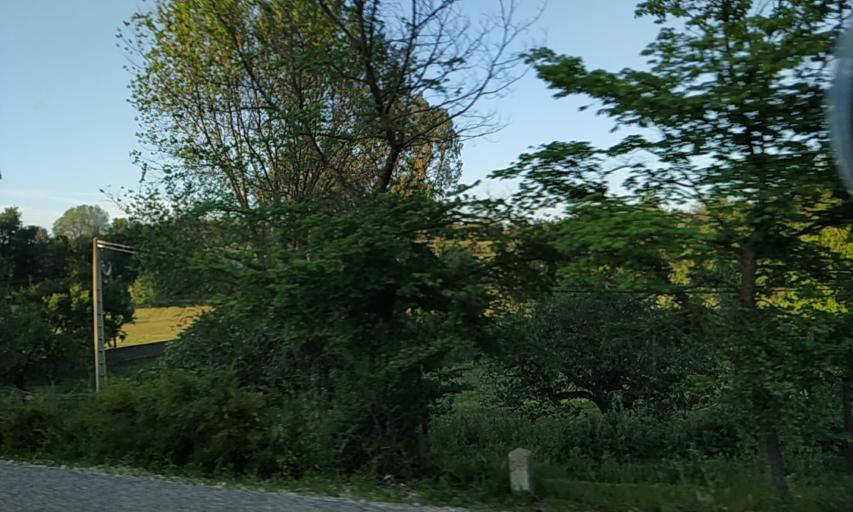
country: ES
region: Extremadura
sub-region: Provincia de Caceres
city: Valencia de Alcantara
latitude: 39.3955
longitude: -7.2474
